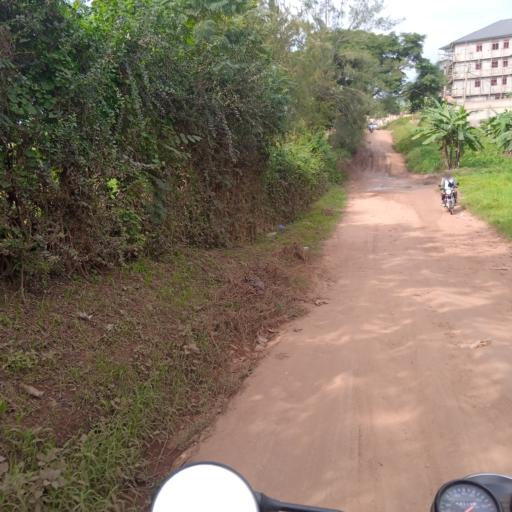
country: UG
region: Eastern Region
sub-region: Mbale District
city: Mbale
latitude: 1.0732
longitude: 34.1848
